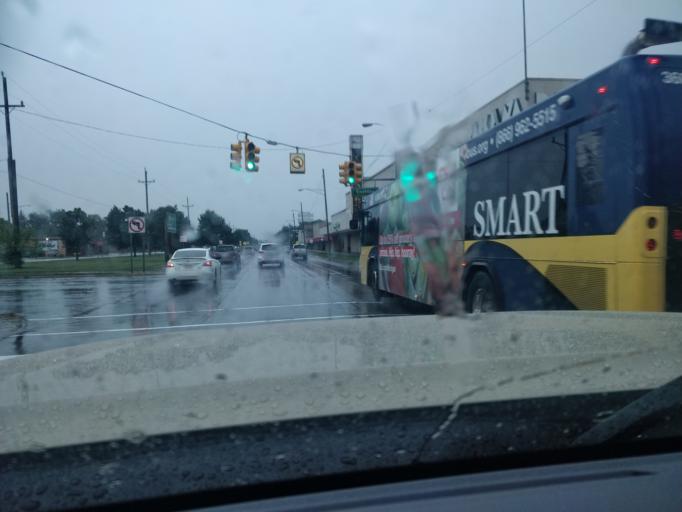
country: US
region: Michigan
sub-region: Wayne County
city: Lincoln Park
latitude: 42.2323
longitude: -83.1806
